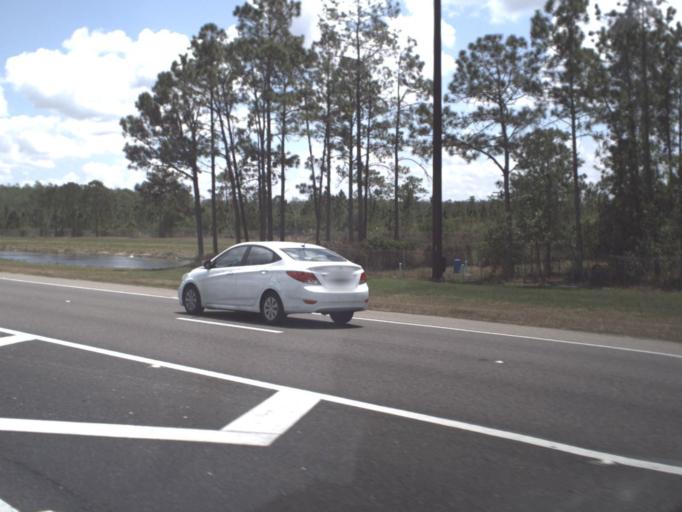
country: US
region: Florida
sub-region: Orange County
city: Alafaya
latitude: 28.4513
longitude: -81.2250
